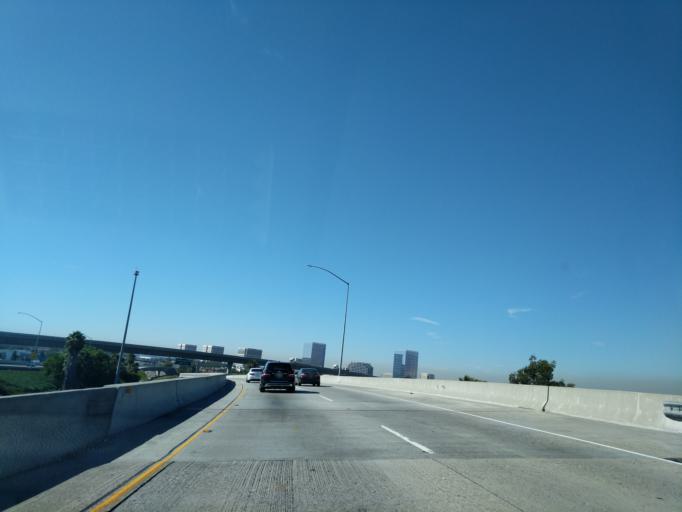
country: US
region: California
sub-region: Orange County
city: Laguna Woods
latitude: 33.6451
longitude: -117.7349
